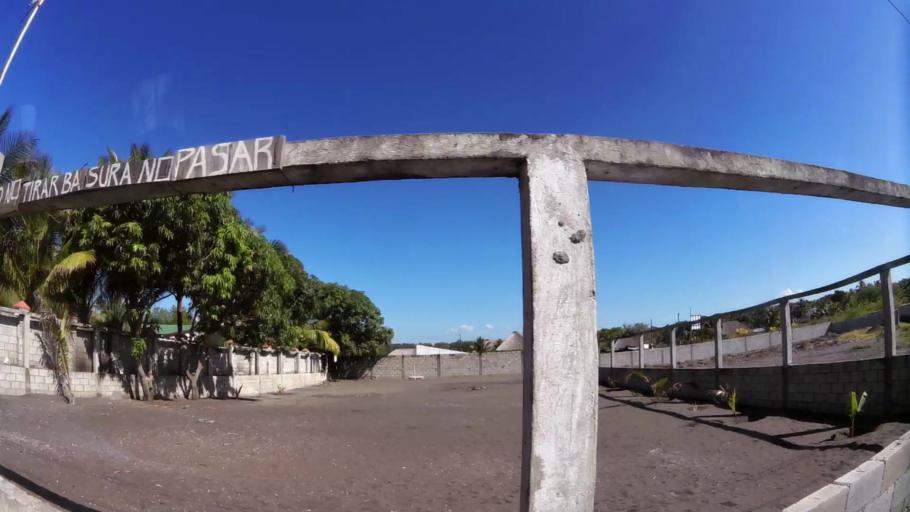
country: GT
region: Santa Rosa
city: Guazacapan
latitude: 13.8658
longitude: -90.4126
